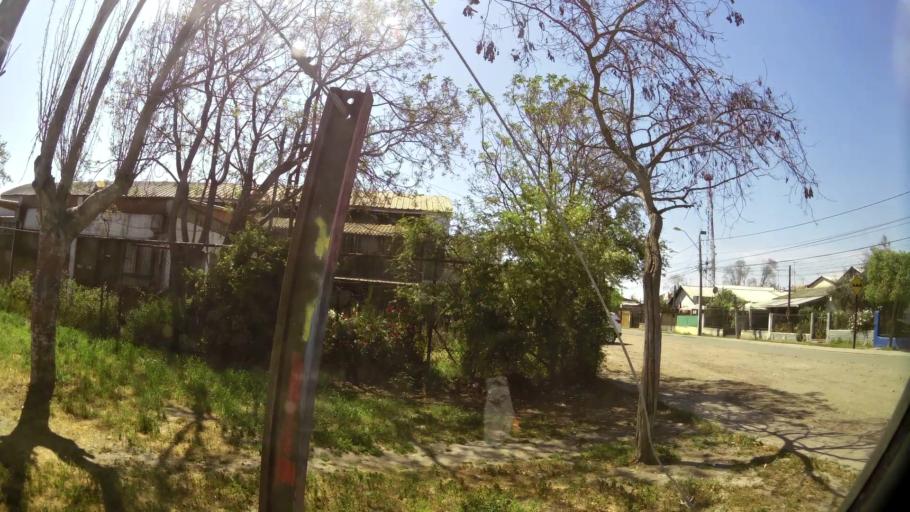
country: CL
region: Santiago Metropolitan
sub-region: Provincia de Talagante
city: Penaflor
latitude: -33.6124
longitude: -70.9026
